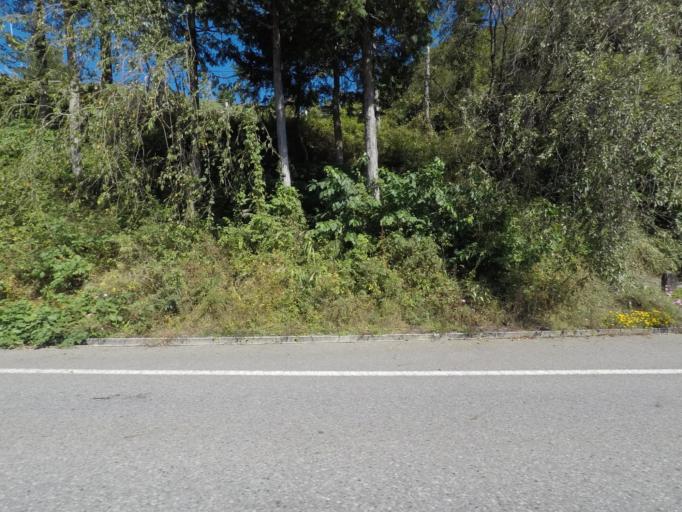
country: JP
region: Nagano
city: Shiojiri
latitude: 35.9823
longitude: 137.7443
